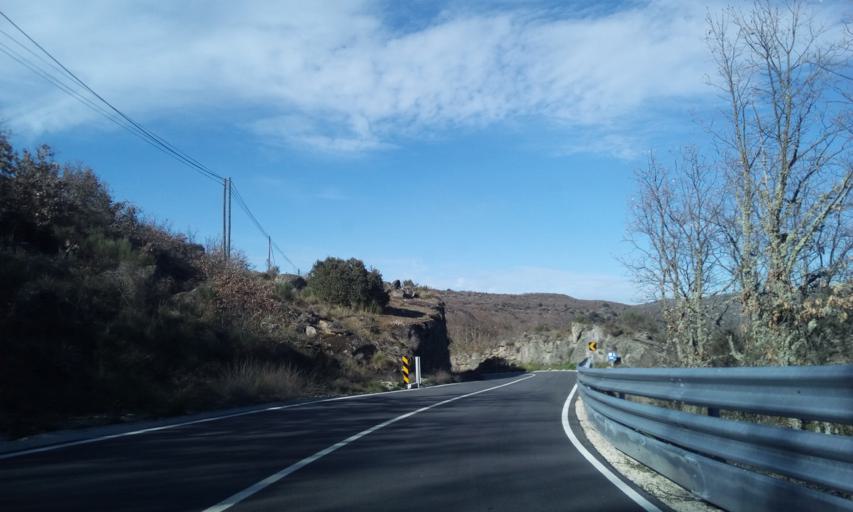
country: ES
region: Castille and Leon
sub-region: Provincia de Salamanca
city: Fuentes de Onoro
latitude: 40.6120
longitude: -6.9209
